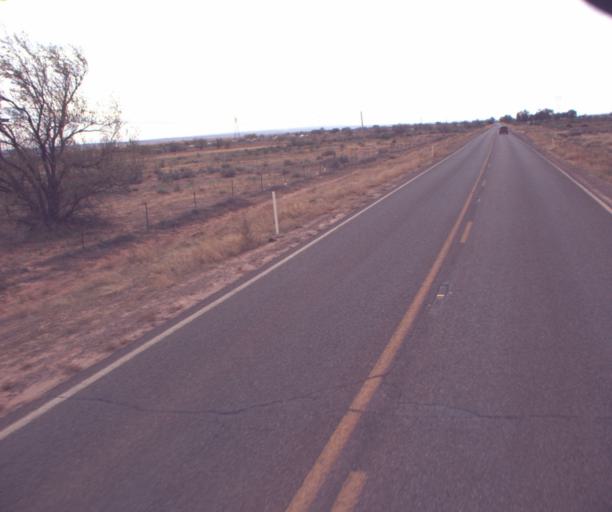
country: US
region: Arizona
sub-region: Apache County
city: Many Farms
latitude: 36.2511
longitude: -109.6054
